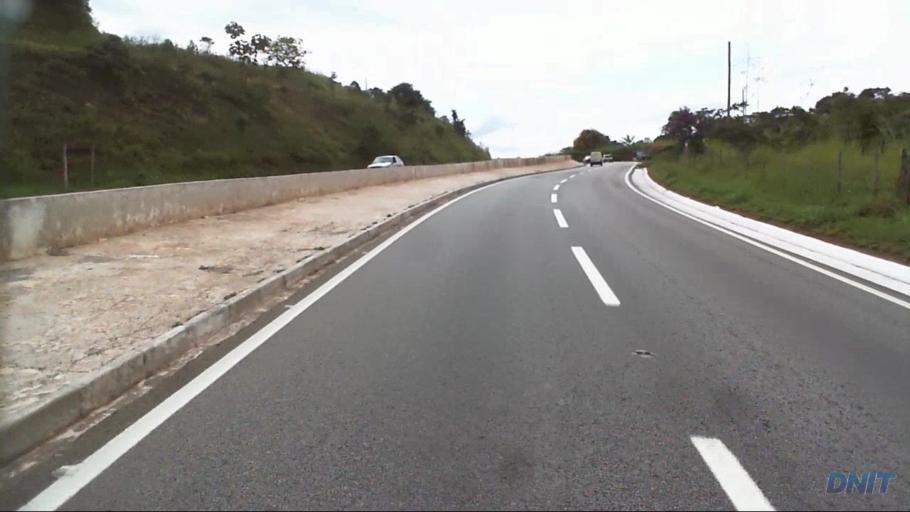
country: BR
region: Minas Gerais
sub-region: Caete
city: Caete
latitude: -19.7892
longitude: -43.6824
